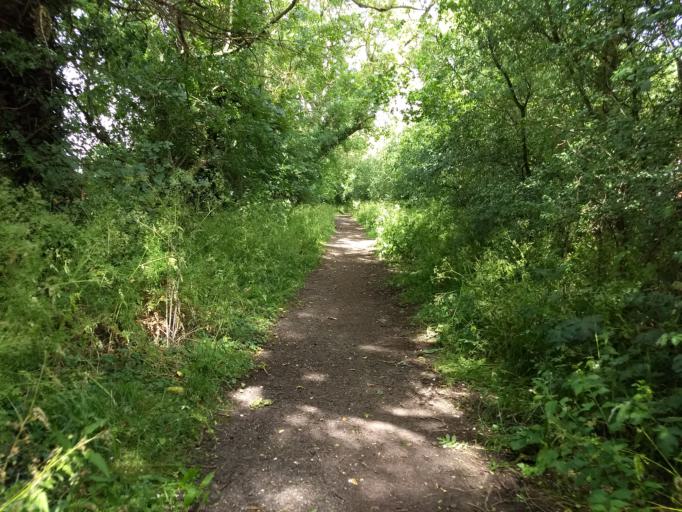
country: GB
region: England
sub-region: Milton Keynes
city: Shenley Church End
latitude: 52.0027
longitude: -0.8096
